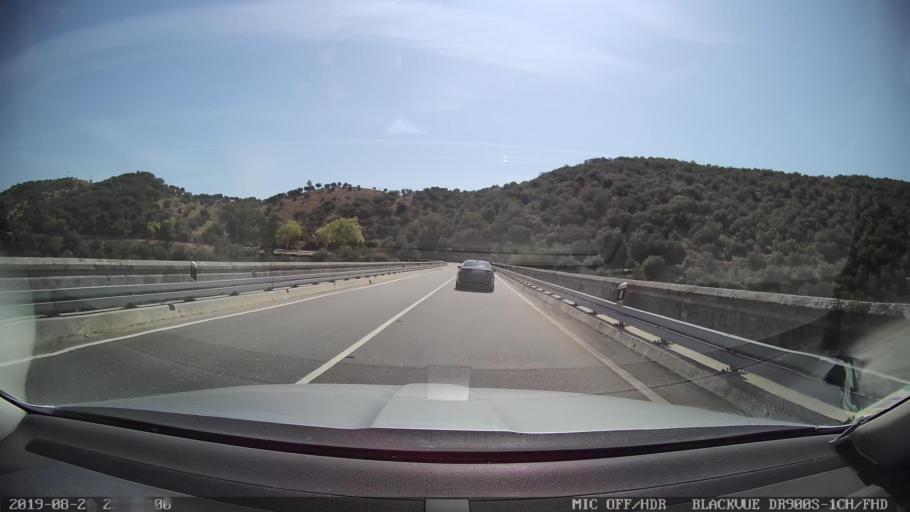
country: PT
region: Castelo Branco
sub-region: Idanha-A-Nova
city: Idanha-a-Nova
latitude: 39.8586
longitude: -7.3342
